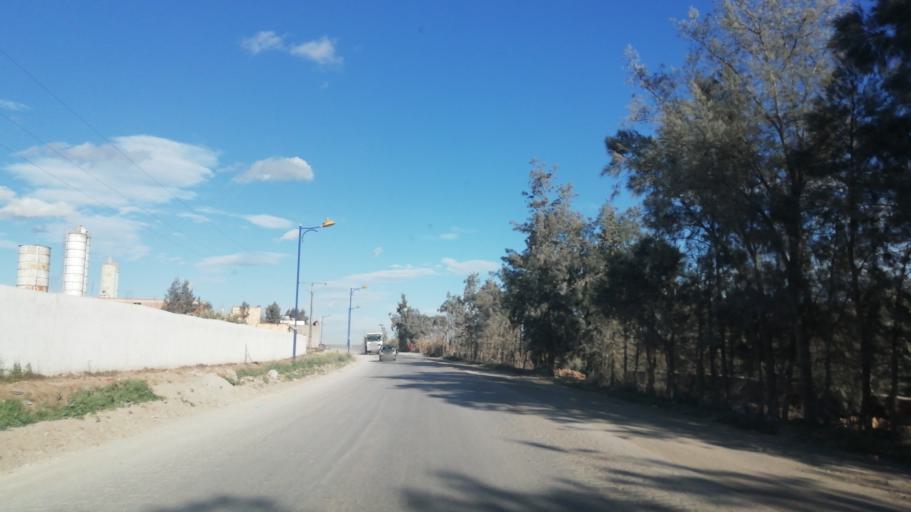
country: DZ
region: Oran
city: Sidi ech Chahmi
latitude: 35.6406
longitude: -0.5407
